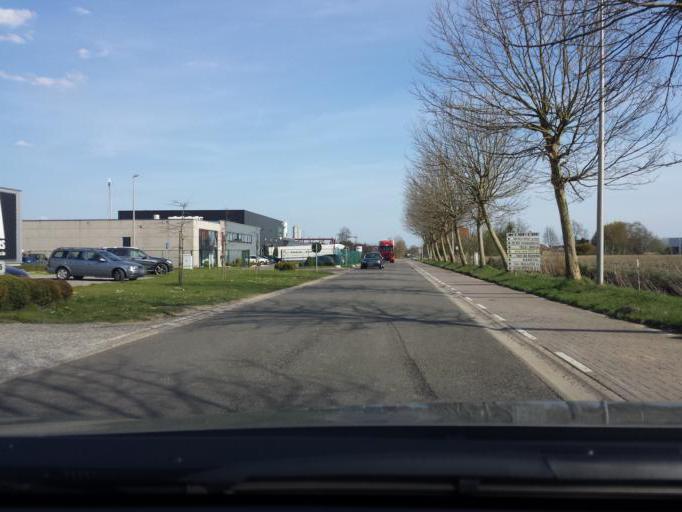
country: BE
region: Flanders
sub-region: Provincie Limburg
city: Halen
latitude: 50.9497
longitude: 5.1008
